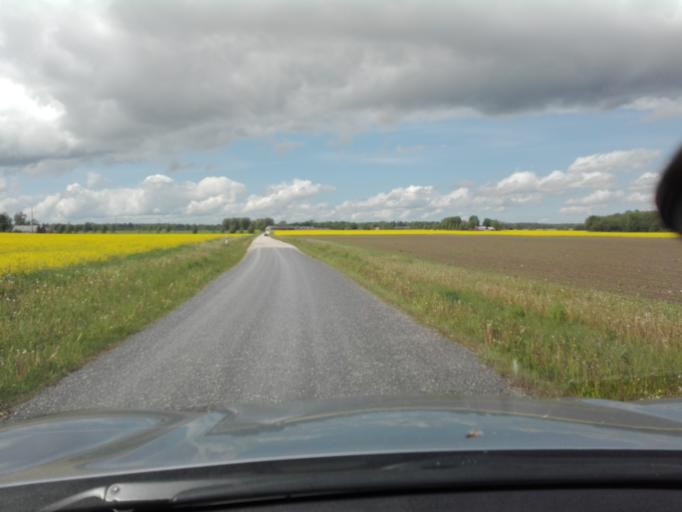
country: EE
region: Raplamaa
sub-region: Kehtna vald
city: Kehtna
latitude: 58.9637
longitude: 24.8893
